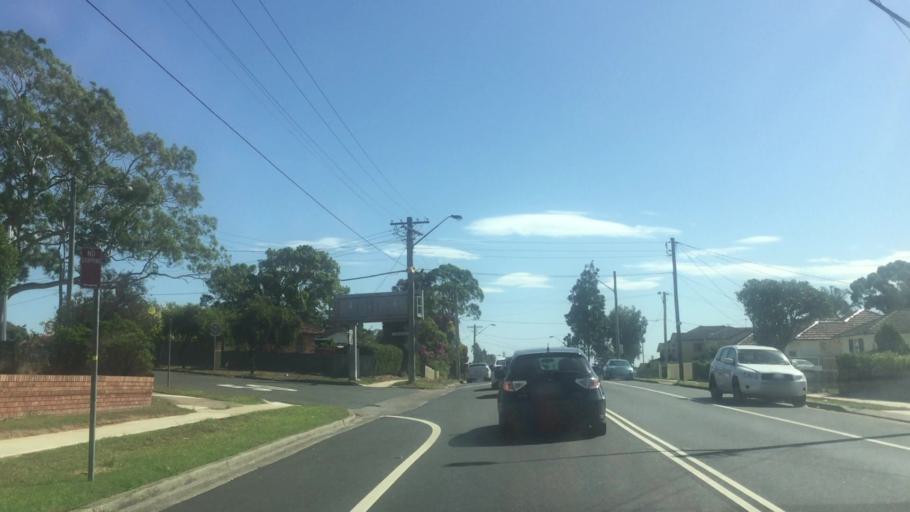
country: AU
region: New South Wales
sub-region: Holroyd
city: Merrylands
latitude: -33.8252
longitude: 150.9858
